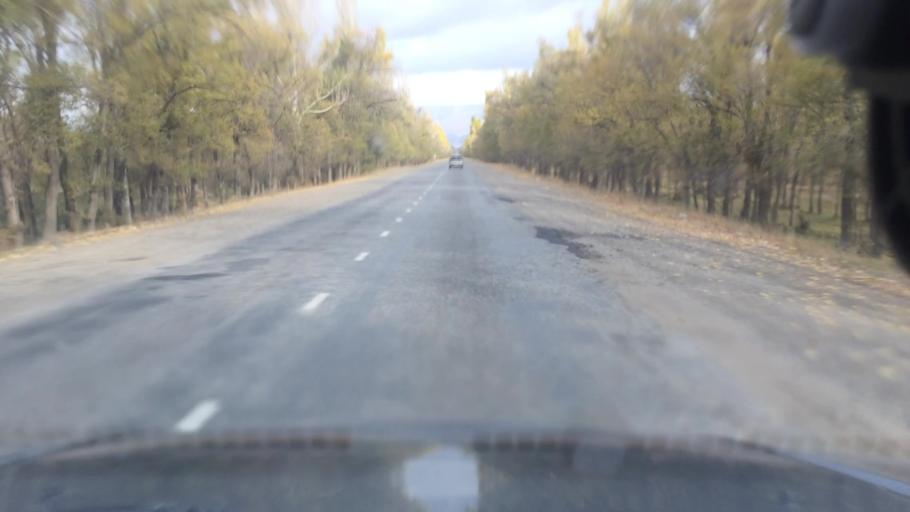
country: KG
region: Ysyk-Koel
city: Tyup
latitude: 42.6304
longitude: 78.3607
